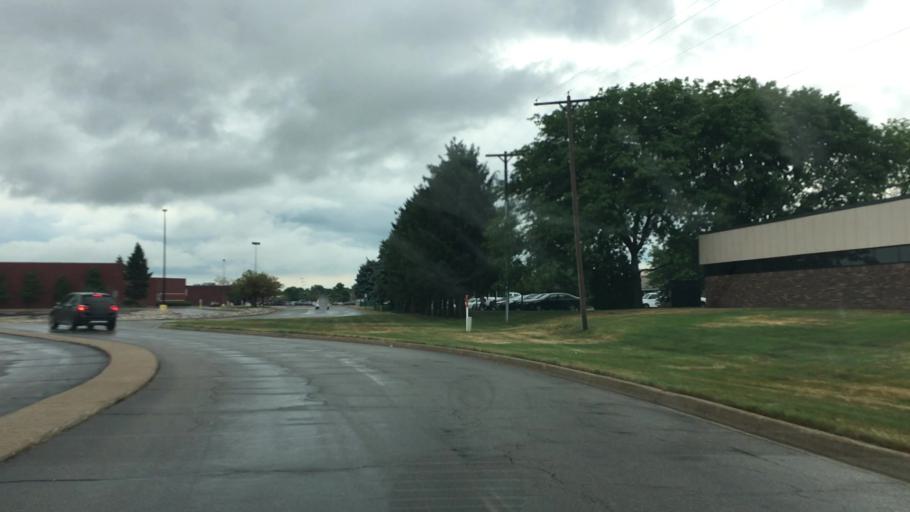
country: US
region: Michigan
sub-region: Ottawa County
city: Holland
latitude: 42.8128
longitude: -86.0860
